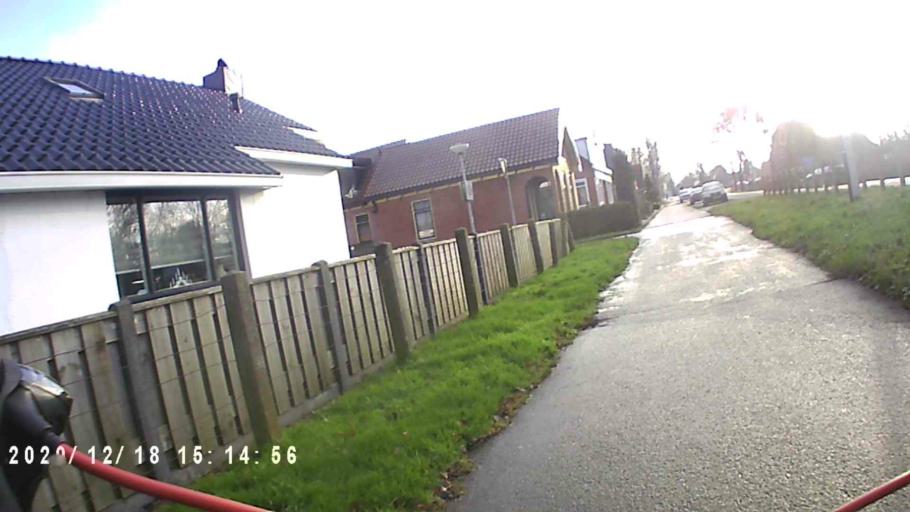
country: NL
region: Groningen
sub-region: Gemeente Hoogezand-Sappemeer
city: Hoogezand
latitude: 53.1630
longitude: 6.7227
